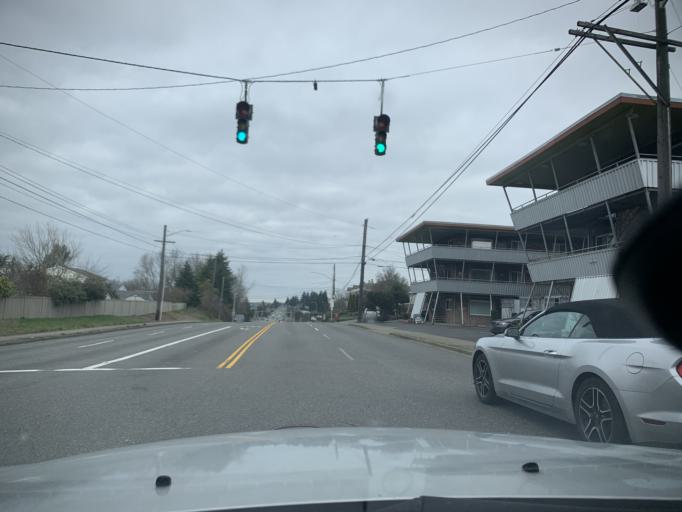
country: US
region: Washington
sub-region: Pierce County
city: University Place
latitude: 47.2556
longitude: -122.5369
